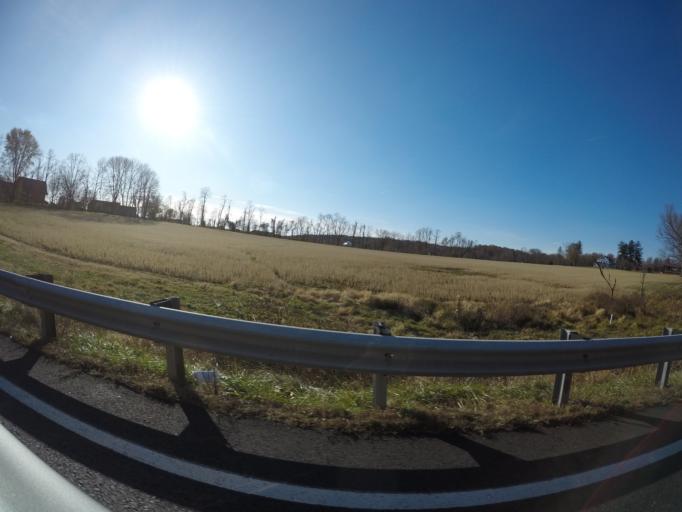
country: US
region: Maryland
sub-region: Harford County
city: South Bel Air
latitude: 39.6191
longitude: -76.2577
